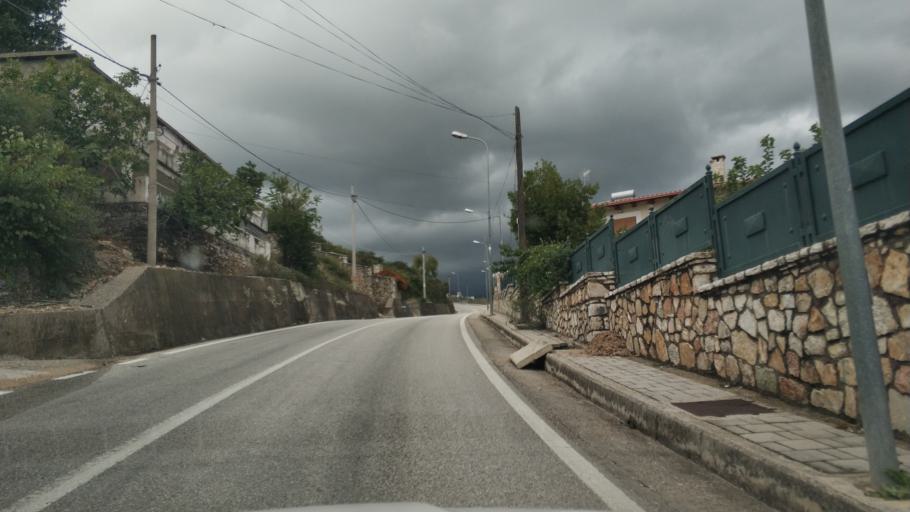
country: AL
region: Vlore
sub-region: Rrethi i Vlores
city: Himare
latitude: 40.1094
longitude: 19.7407
